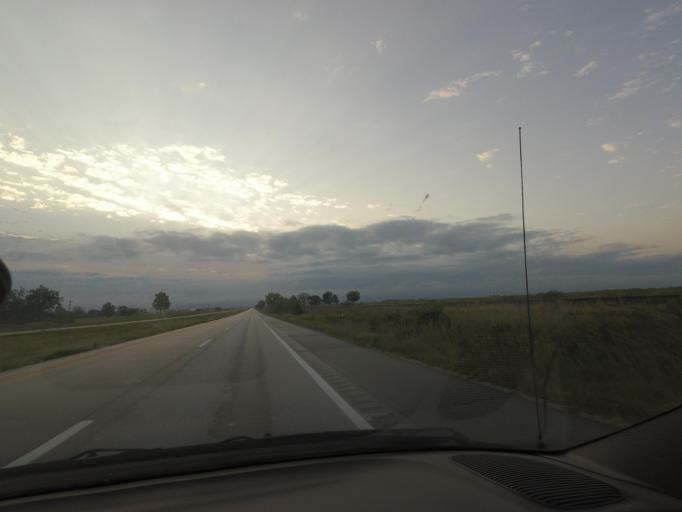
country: US
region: Missouri
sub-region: Shelby County
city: Shelbina
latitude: 39.7117
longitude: -92.1172
